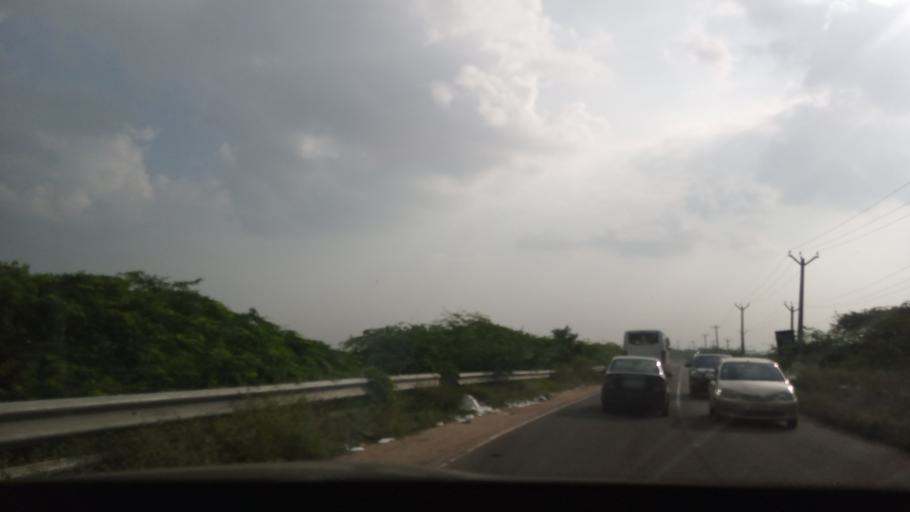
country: IN
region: Tamil Nadu
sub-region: Kancheepuram
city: Vengavasal
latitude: 12.7842
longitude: 80.2319
